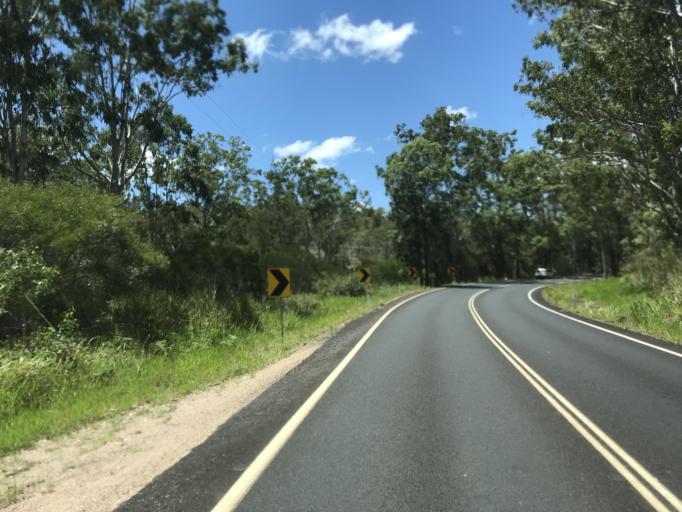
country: AU
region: Queensland
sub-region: Tablelands
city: Atherton
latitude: -17.4062
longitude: 145.3891
